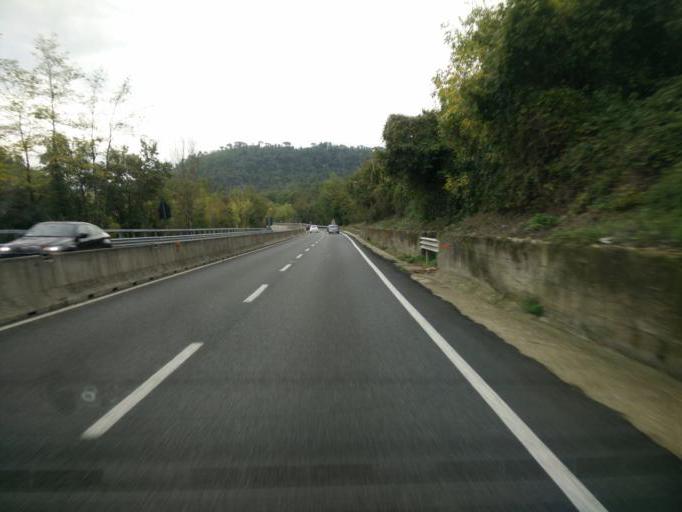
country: IT
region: Tuscany
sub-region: Province of Florence
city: San Casciano in Val di Pesa
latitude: 43.6782
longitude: 11.2109
